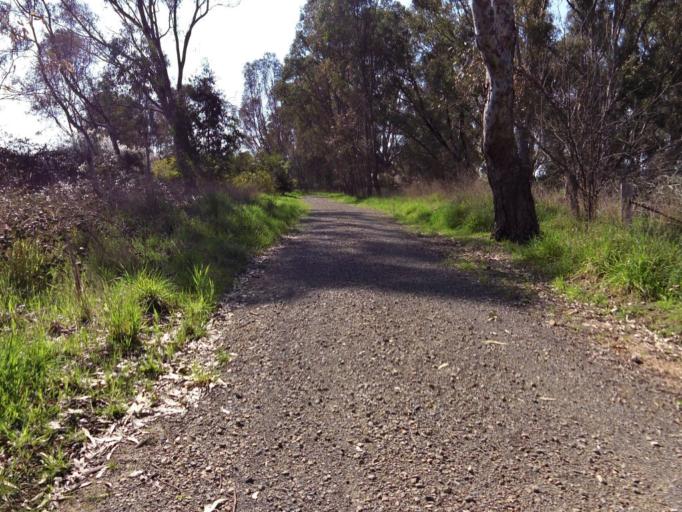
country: AU
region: Victoria
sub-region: Murrindindi
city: Alexandra
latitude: -37.1512
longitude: 145.5810
